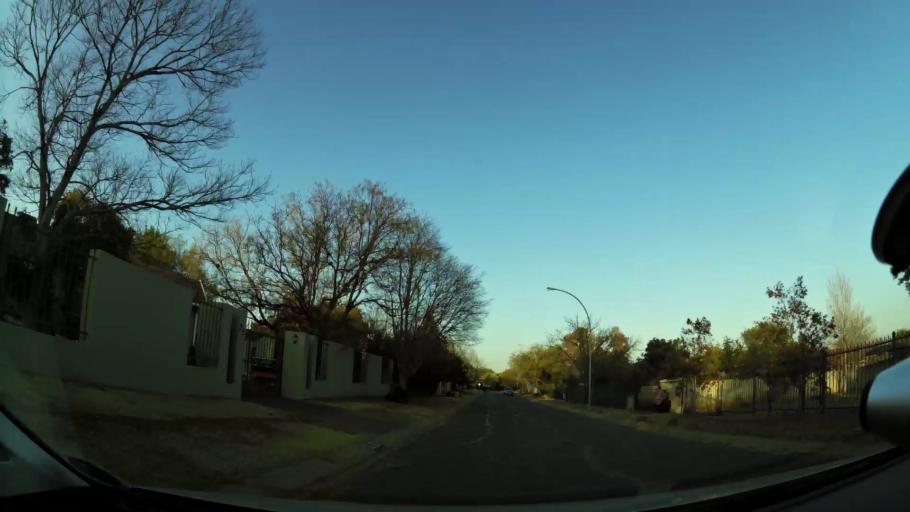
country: ZA
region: Orange Free State
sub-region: Mangaung Metropolitan Municipality
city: Bloemfontein
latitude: -29.0924
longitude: 26.1526
